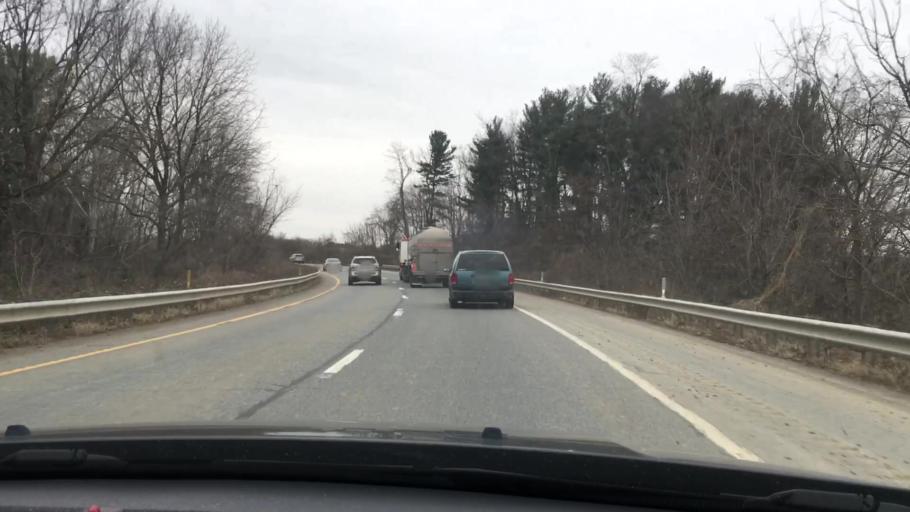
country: US
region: Pennsylvania
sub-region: Lancaster County
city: Willow Street
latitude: 39.9681
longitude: -76.2769
